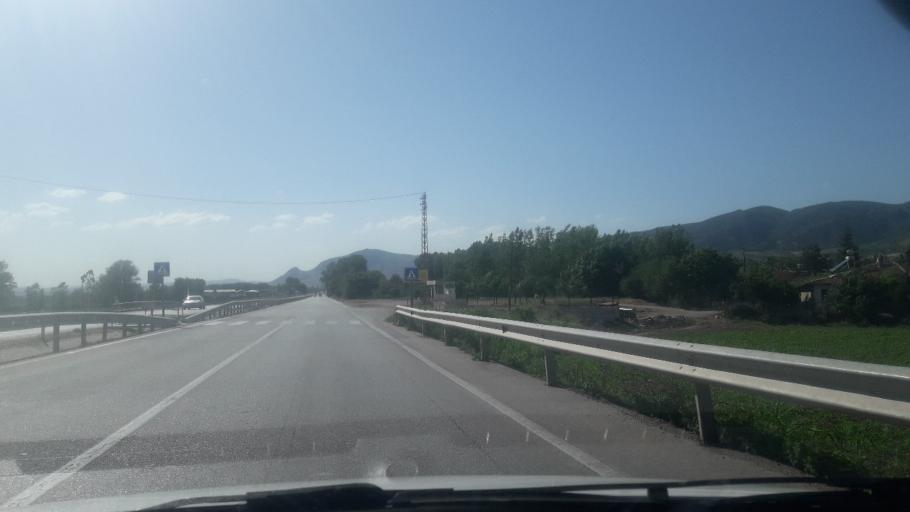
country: TR
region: Tokat
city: Dokmetepe
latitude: 40.3093
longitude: 36.2934
